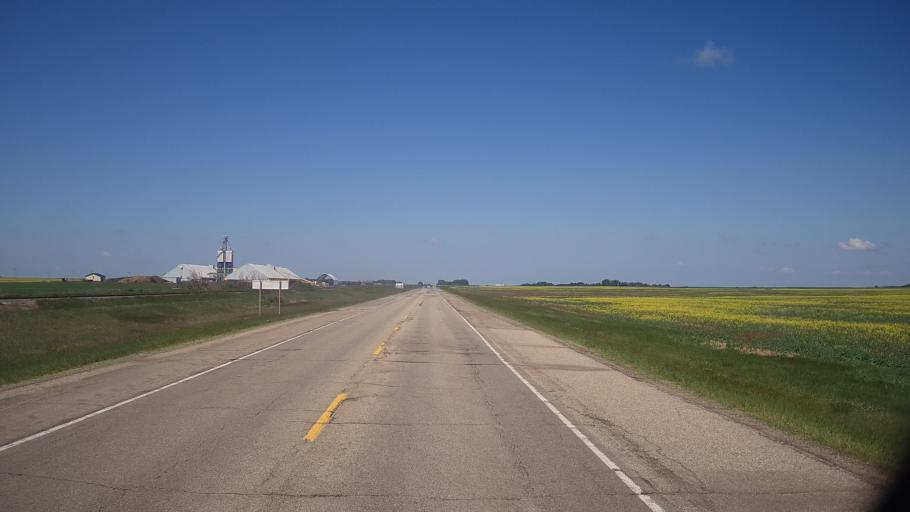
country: CA
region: Saskatchewan
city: Saskatoon
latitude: 51.9920
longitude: -106.0801
